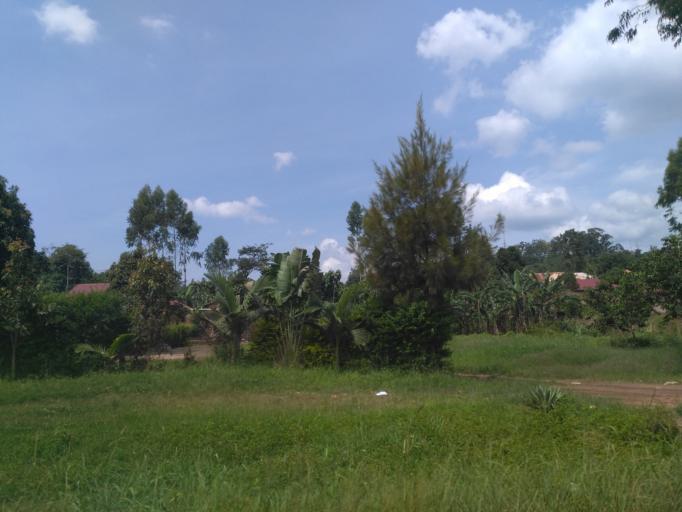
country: UG
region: Central Region
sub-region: Wakiso District
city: Bweyogerere
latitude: 0.4862
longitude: 32.6101
